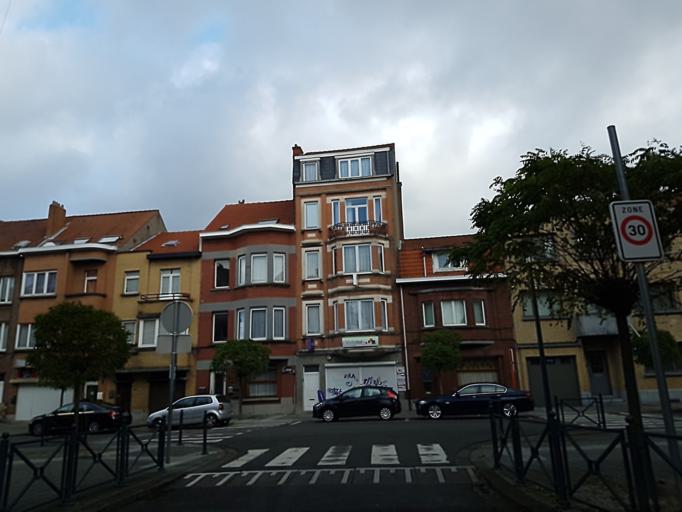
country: BE
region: Flanders
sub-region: Provincie Vlaams-Brabant
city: Diegem
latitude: 50.8704
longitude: 4.3998
